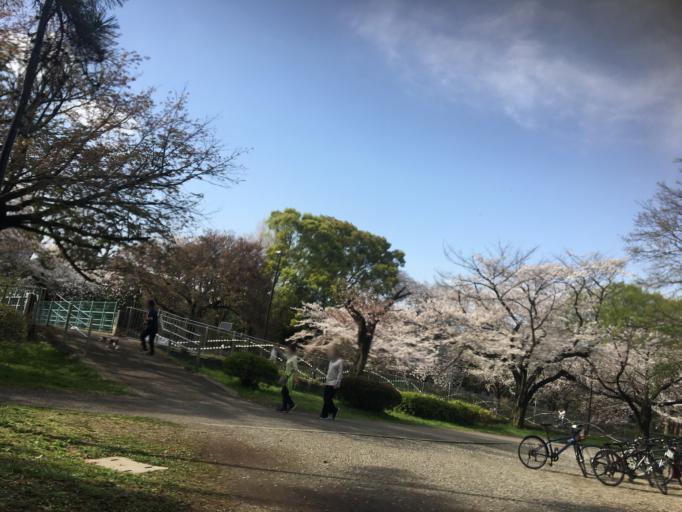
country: JP
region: Tokyo
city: Tokyo
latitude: 35.6919
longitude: 139.6278
